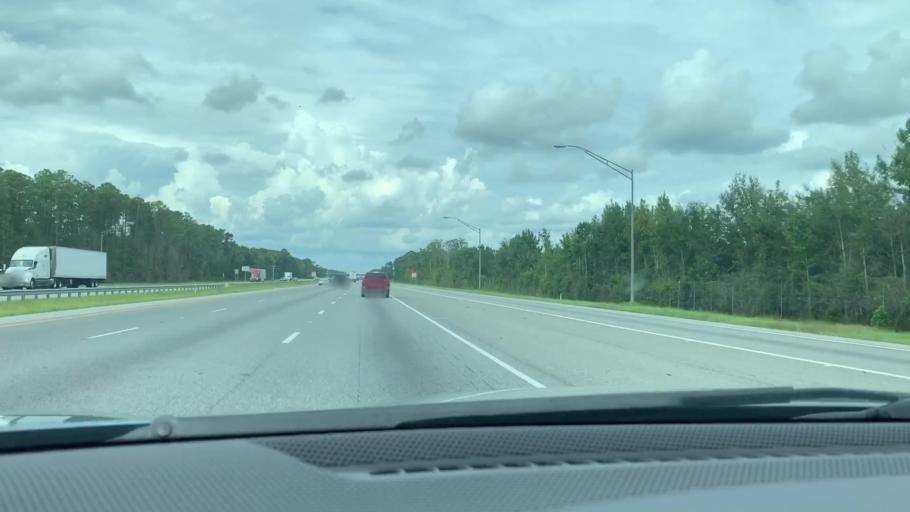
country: US
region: Georgia
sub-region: McIntosh County
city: Darien
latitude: 31.4829
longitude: -81.4471
